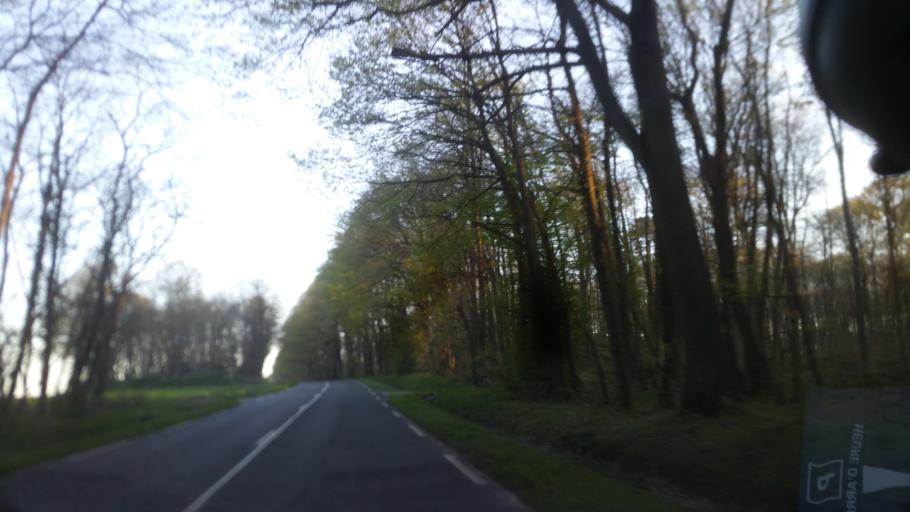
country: FR
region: Ile-de-France
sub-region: Departement de l'Essonne
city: Angervilliers
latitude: 48.6186
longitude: 2.0731
